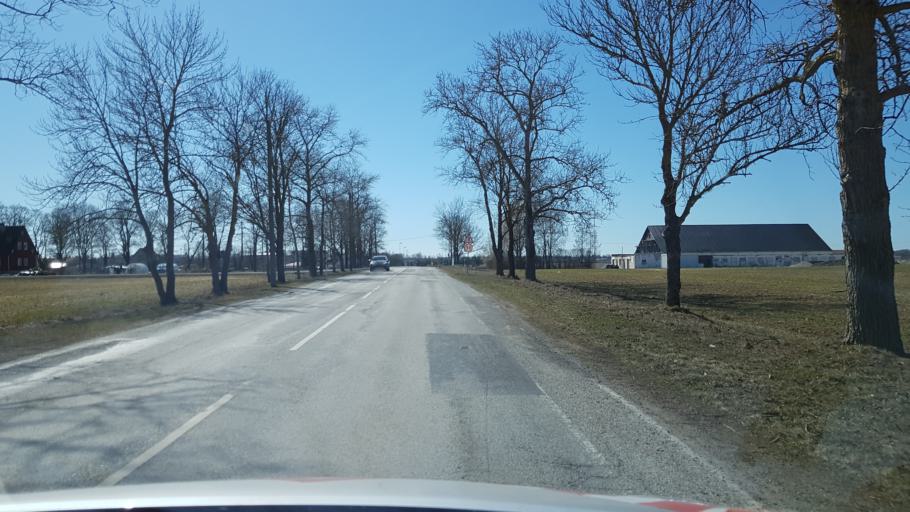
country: EE
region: Laeaene-Virumaa
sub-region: Rakvere linn
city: Rakvere
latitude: 59.3674
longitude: 26.3746
